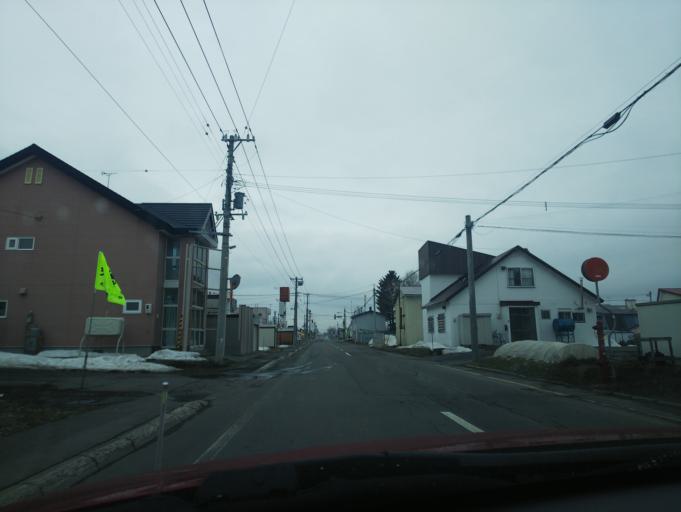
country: JP
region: Hokkaido
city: Nayoro
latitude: 44.3625
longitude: 142.4502
